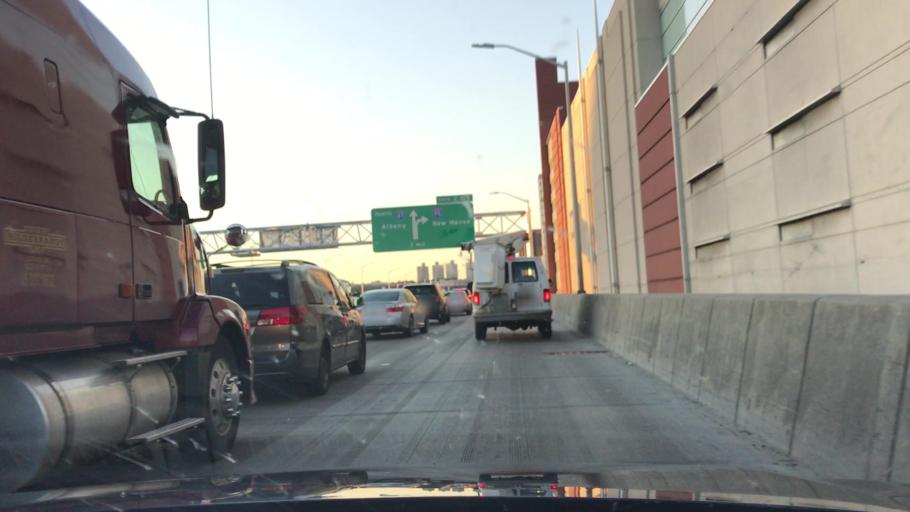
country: US
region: New York
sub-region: New York County
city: Inwood
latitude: 40.8212
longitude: -73.9307
